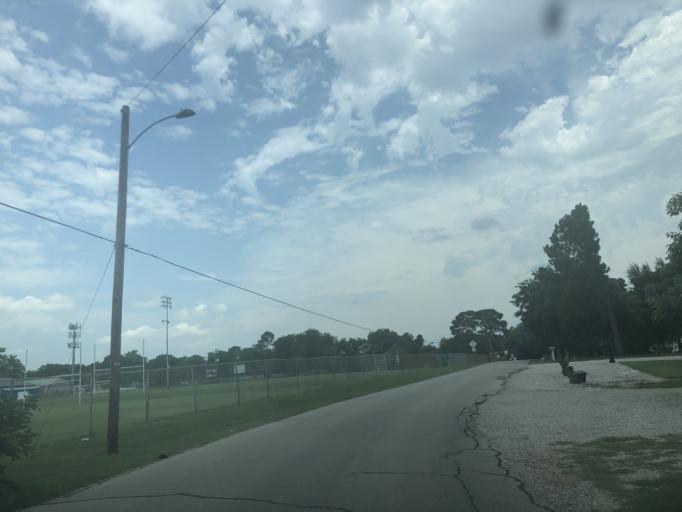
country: US
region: Texas
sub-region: Dallas County
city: Irving
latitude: 32.7922
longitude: -96.9430
